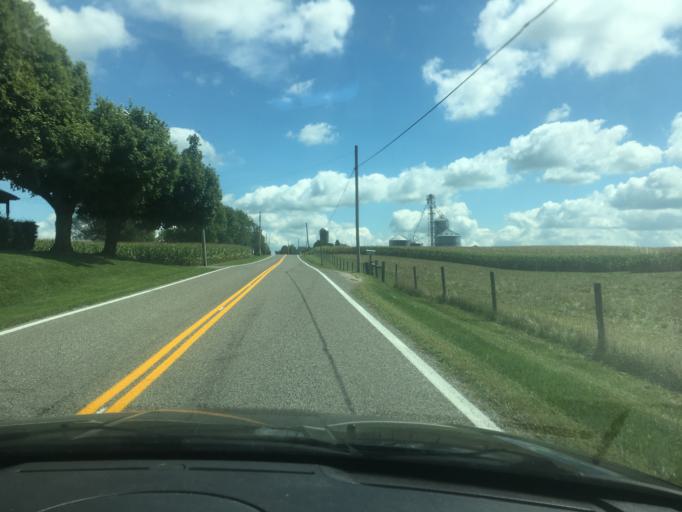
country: US
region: Ohio
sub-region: Logan County
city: West Liberty
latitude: 40.2324
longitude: -83.7174
